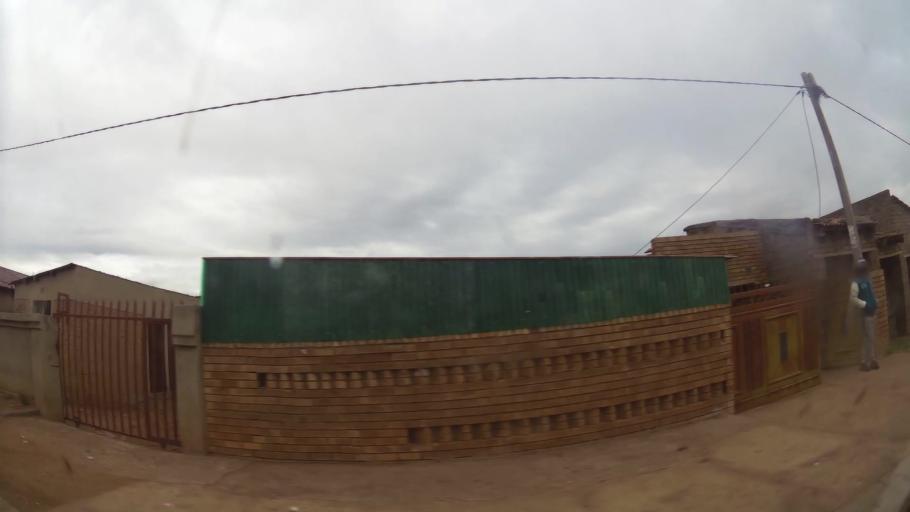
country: ZA
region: Gauteng
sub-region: Ekurhuleni Metropolitan Municipality
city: Germiston
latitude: -26.3802
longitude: 28.1733
